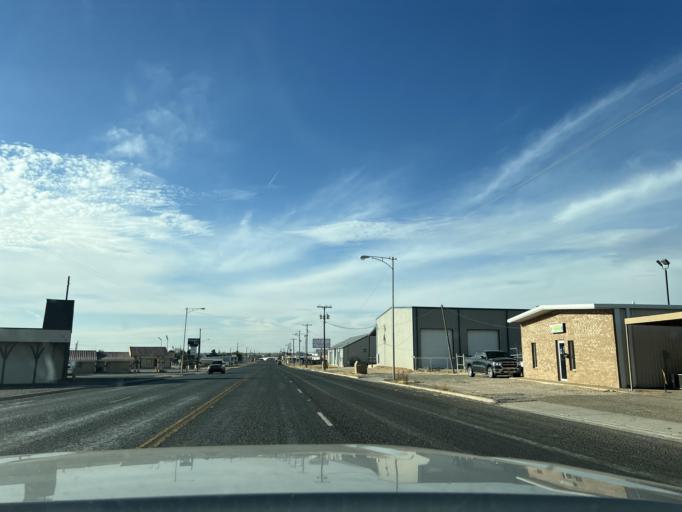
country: US
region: Texas
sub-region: Scurry County
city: Snyder
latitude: 32.7147
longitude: -100.8979
